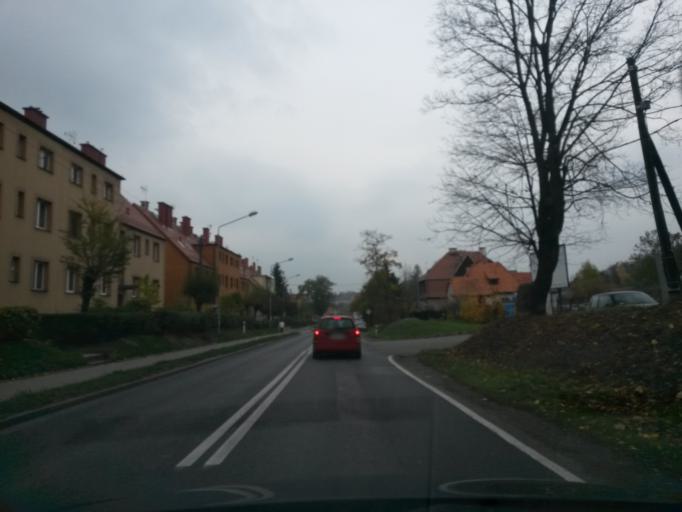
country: PL
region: Lower Silesian Voivodeship
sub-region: Powiat klodzki
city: Klodzko
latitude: 50.4273
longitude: 16.6587
